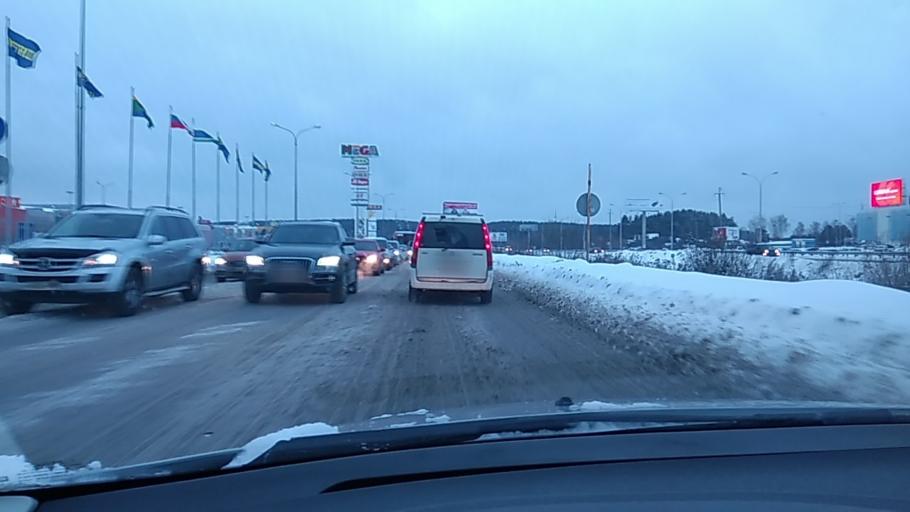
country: RU
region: Sverdlovsk
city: Shirokaya Rechka
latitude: 56.8262
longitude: 60.5120
